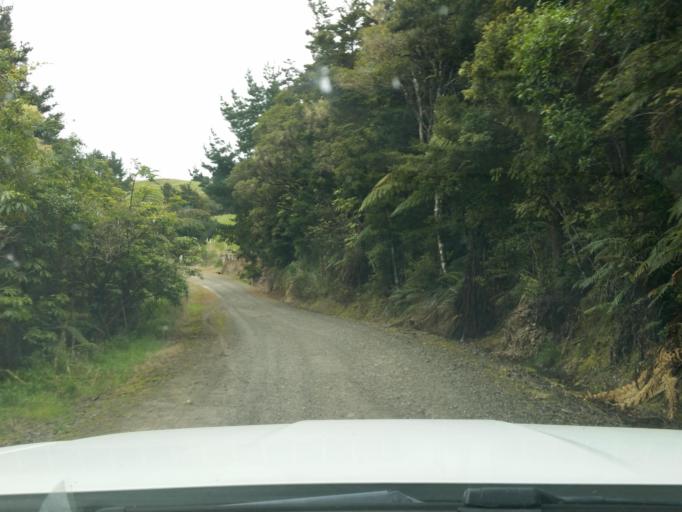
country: NZ
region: Northland
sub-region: Kaipara District
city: Dargaville
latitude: -35.7068
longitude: 173.6242
